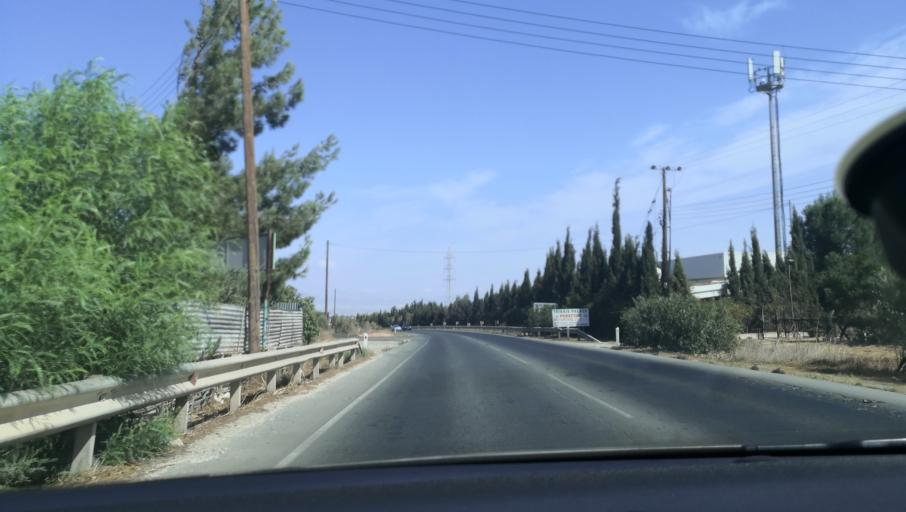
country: CY
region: Lefkosia
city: Kato Deftera
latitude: 35.0965
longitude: 33.2853
